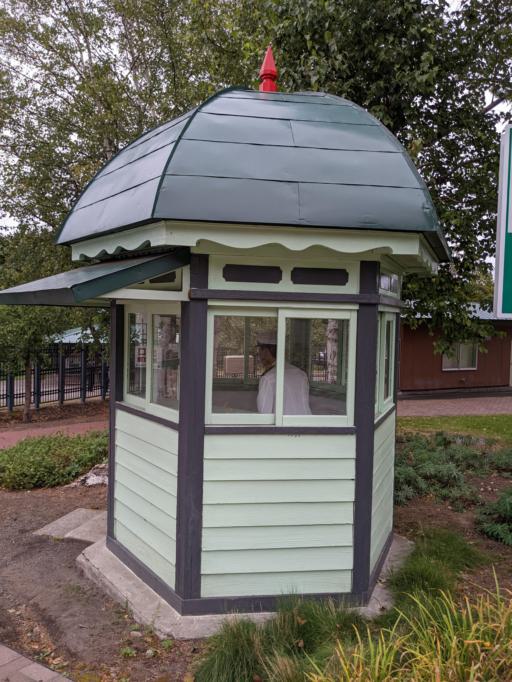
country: JP
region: Hokkaido
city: Abashiri
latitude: 43.9958
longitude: 144.2287
